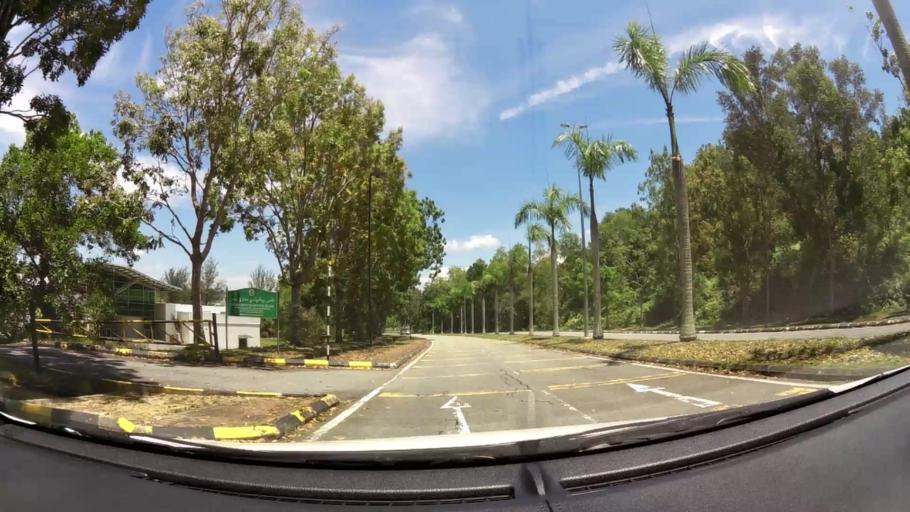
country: BN
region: Brunei and Muara
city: Bandar Seri Begawan
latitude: 4.9228
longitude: 114.9481
